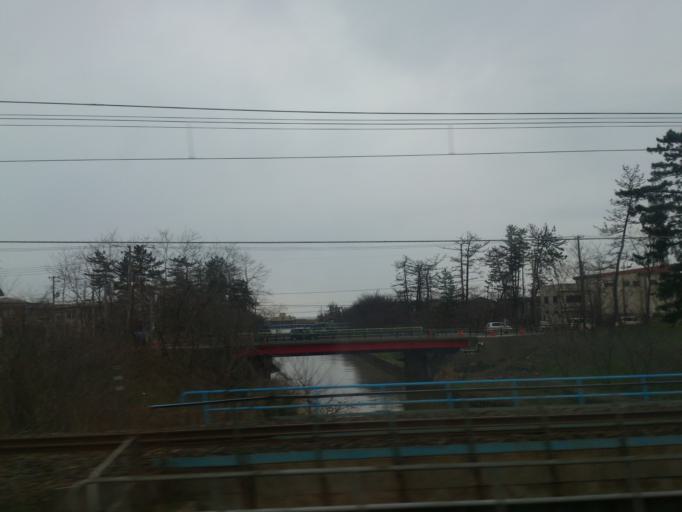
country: JP
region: Niigata
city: Joetsu
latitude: 37.2126
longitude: 138.3090
